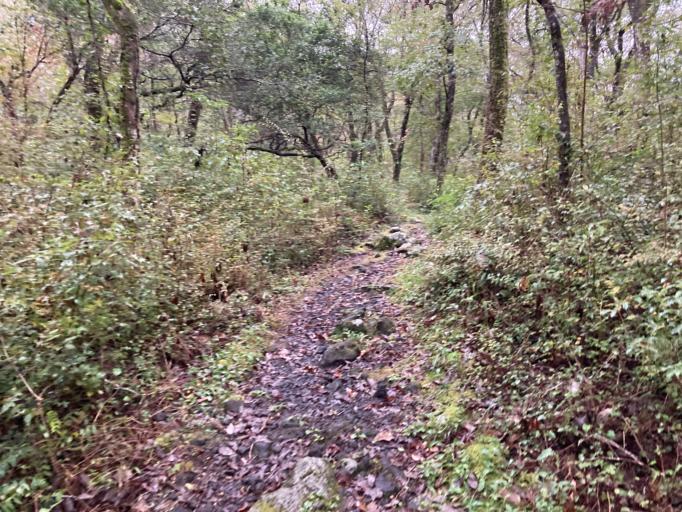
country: JP
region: Shizuoka
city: Fuji
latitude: 35.2421
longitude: 138.7286
